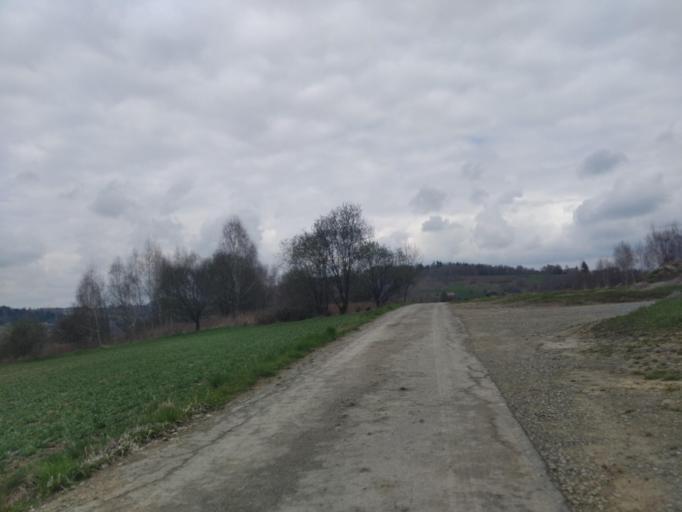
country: PL
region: Subcarpathian Voivodeship
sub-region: Powiat strzyzowski
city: Wysoka Strzyzowska
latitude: 49.8828
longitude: 21.7188
